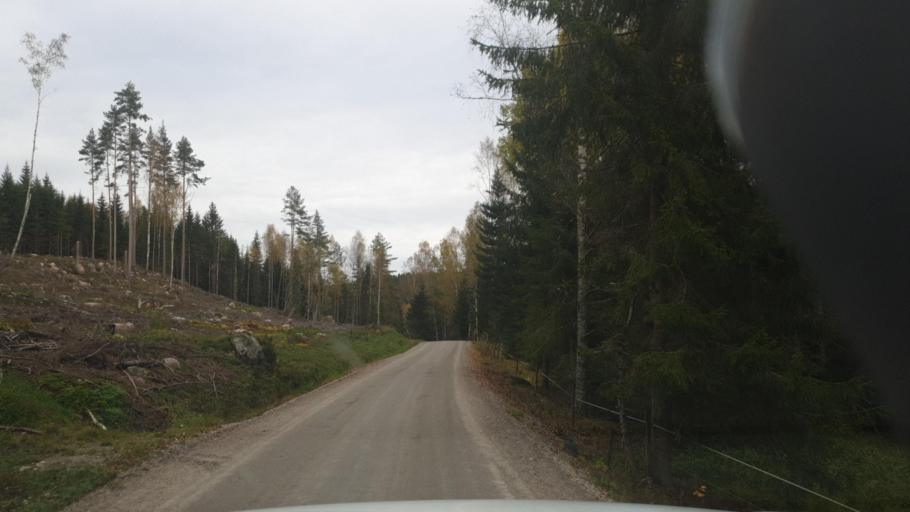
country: SE
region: Vaermland
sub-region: Arvika Kommun
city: Arvika
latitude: 59.6789
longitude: 12.7691
